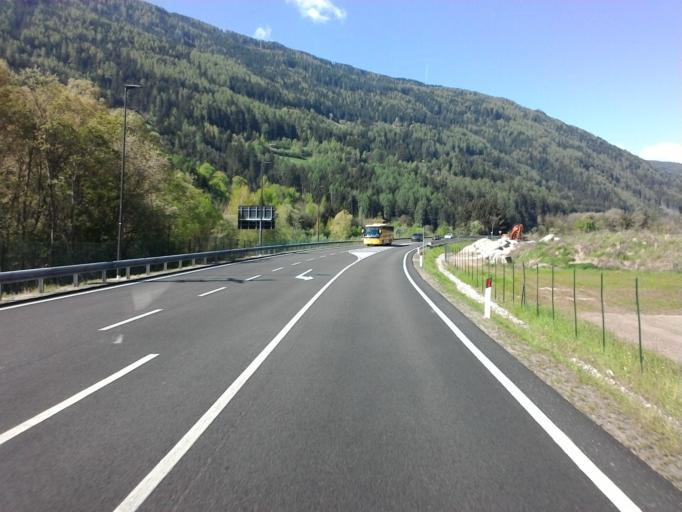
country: IT
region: Trentino-Alto Adige
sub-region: Bolzano
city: Terento
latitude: 46.8113
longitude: 11.7765
